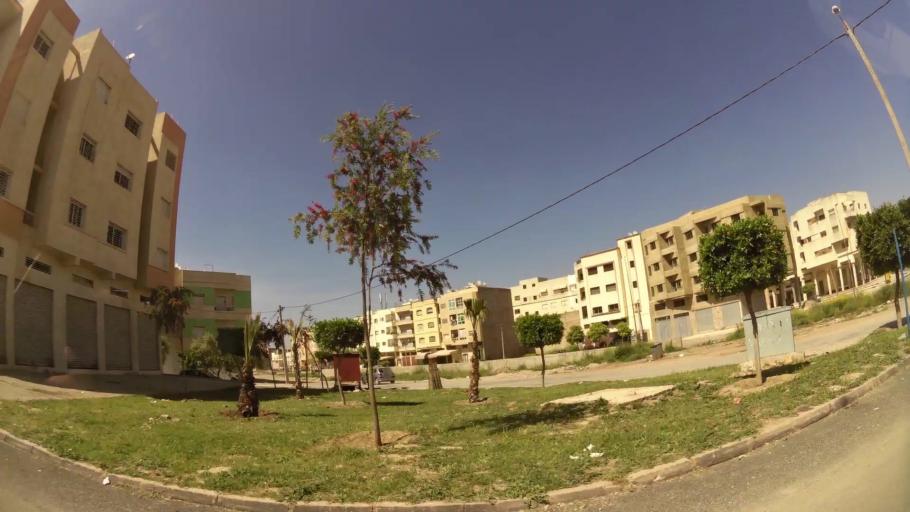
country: MA
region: Fes-Boulemane
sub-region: Fes
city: Fes
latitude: 34.0067
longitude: -5.0320
